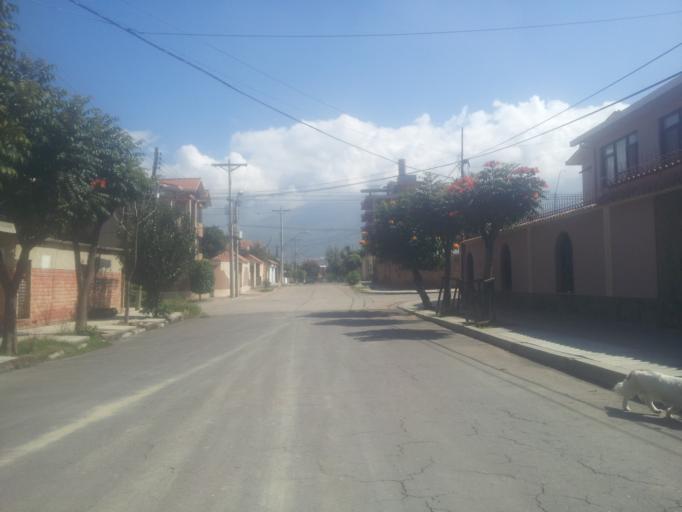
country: BO
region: Cochabamba
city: Cochabamba
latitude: -17.3814
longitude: -66.1729
